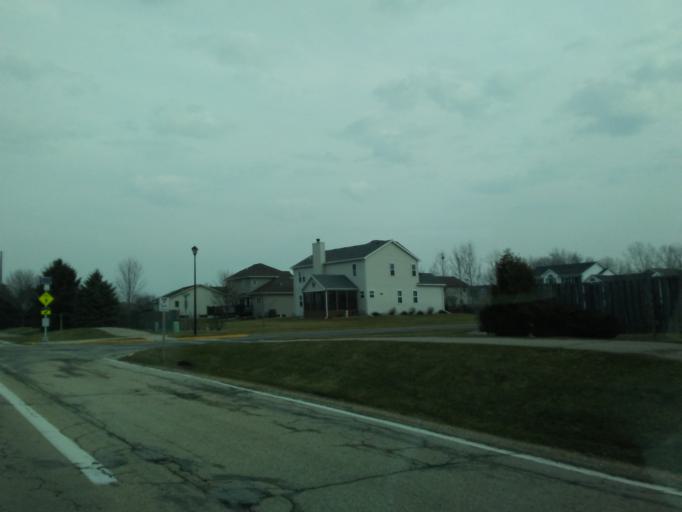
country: US
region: Wisconsin
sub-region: Dane County
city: Waunakee
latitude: 43.2013
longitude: -89.4617
